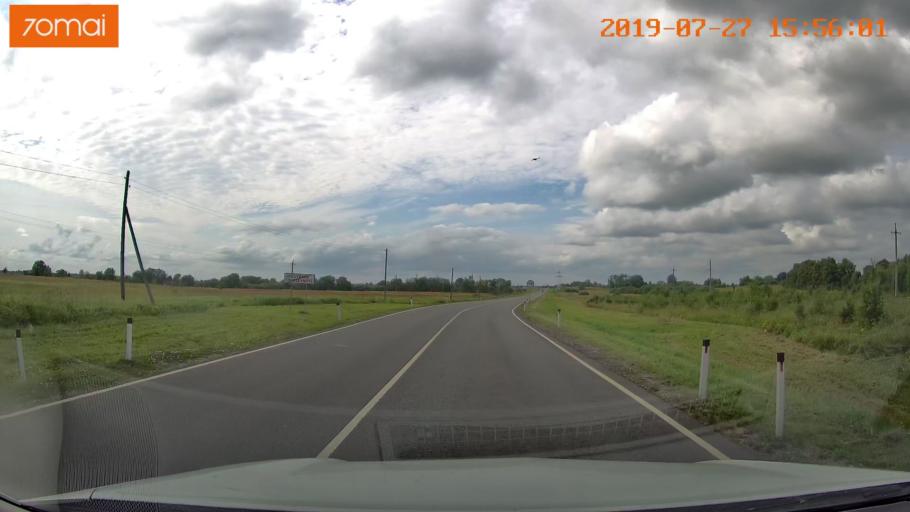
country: RU
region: Kaliningrad
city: Chernyakhovsk
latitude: 54.6162
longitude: 21.9097
